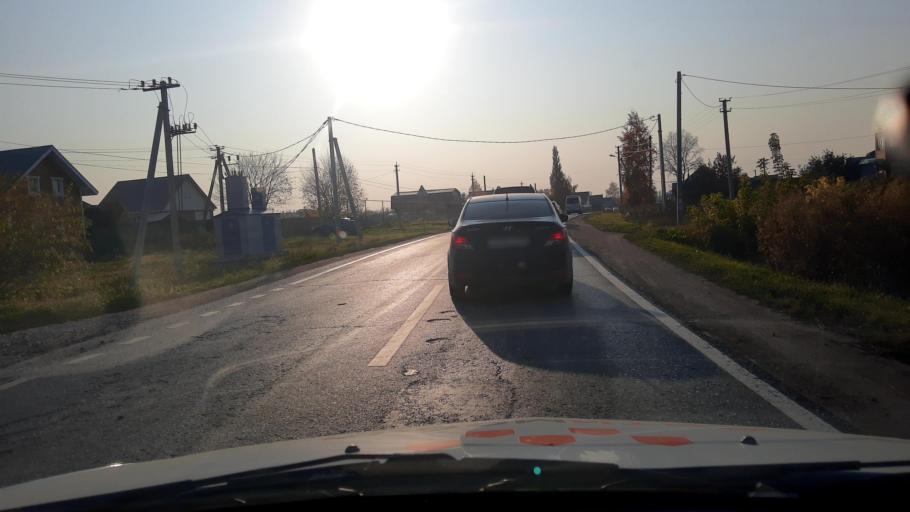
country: RU
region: Bashkortostan
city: Kabakovo
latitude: 54.7468
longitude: 56.2094
